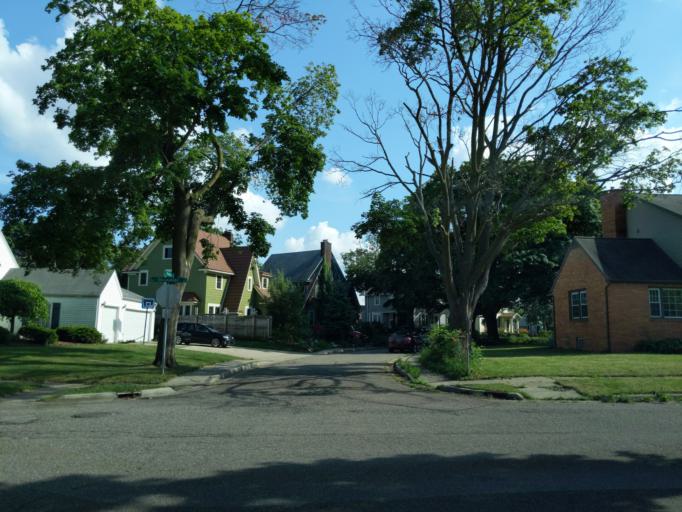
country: US
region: Michigan
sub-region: Ingham County
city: Lansing
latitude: 42.7370
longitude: -84.5753
